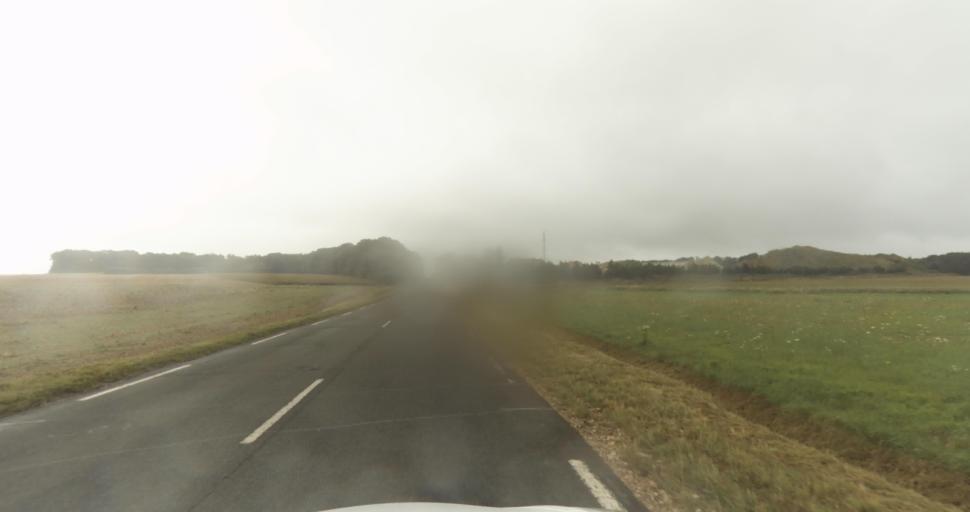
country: FR
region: Haute-Normandie
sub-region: Departement de l'Eure
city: Normanville
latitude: 49.0964
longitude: 1.1748
